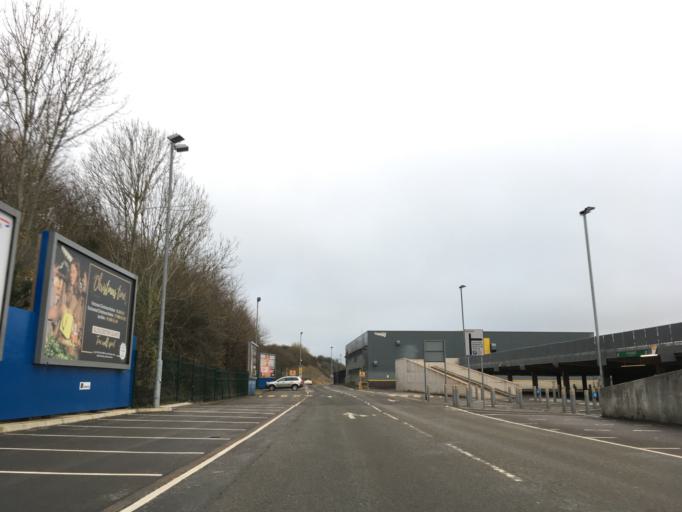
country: GB
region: England
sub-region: South Gloucestershire
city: Stoke Gifford
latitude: 51.5144
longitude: -2.5414
